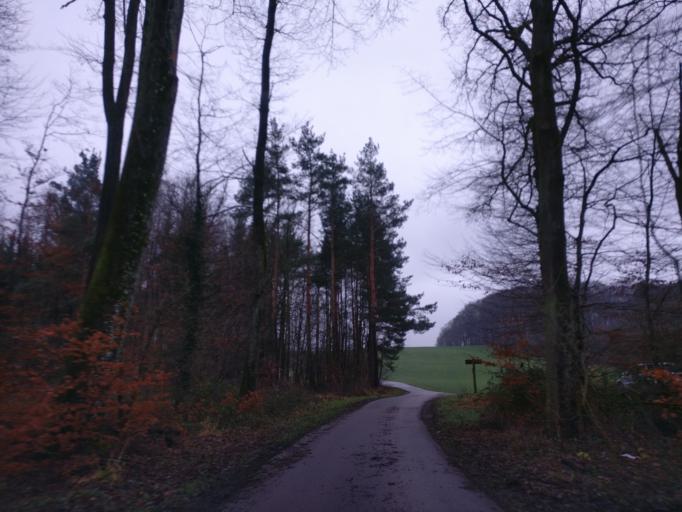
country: DE
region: Baden-Wuerttemberg
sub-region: Regierungsbezirk Stuttgart
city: Rudersberg
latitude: 48.8747
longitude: 9.4940
